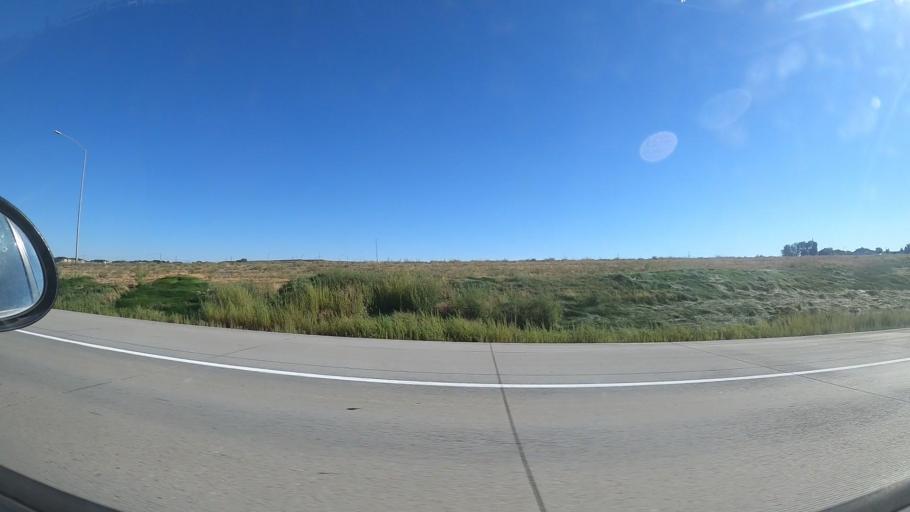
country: US
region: Idaho
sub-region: Ada County
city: Meridian
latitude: 43.5933
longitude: -116.4368
